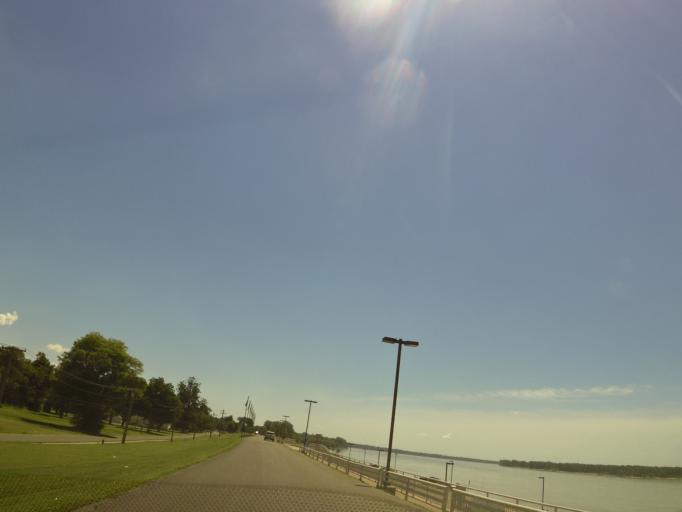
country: US
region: Missouri
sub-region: New Madrid County
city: New Madrid
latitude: 36.5835
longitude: -89.5348
